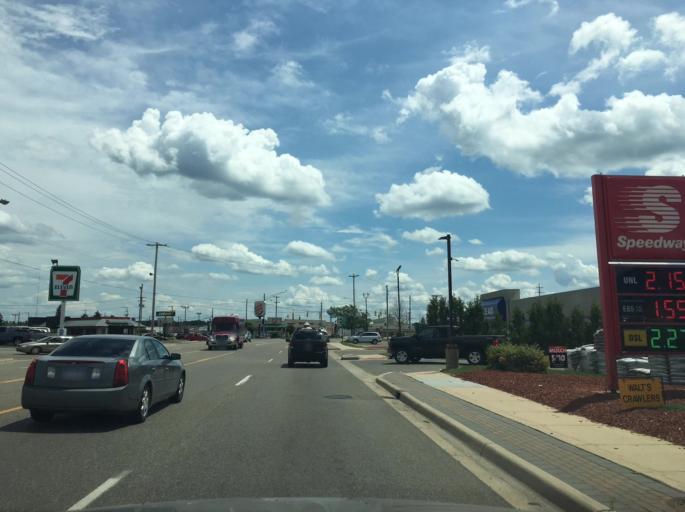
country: US
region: Michigan
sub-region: Crawford County
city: Grayling
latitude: 44.6575
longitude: -84.7096
